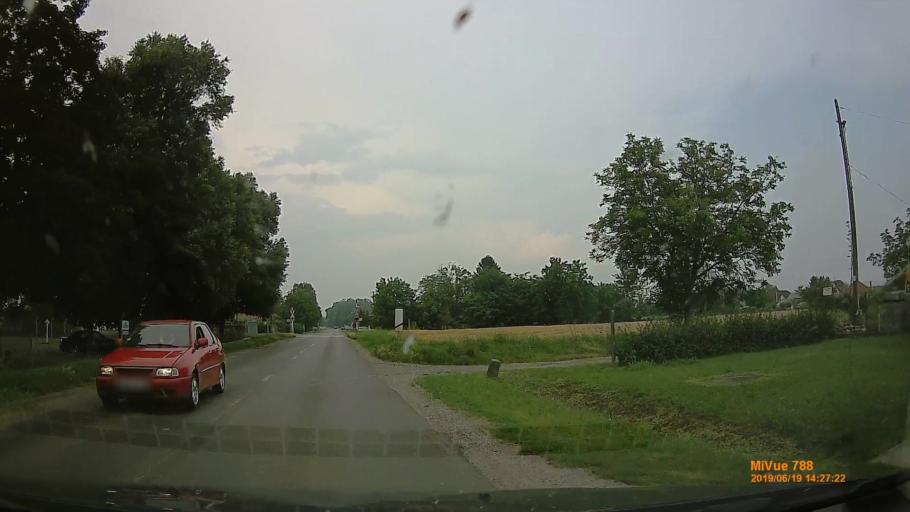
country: HU
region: Baranya
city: Szigetvar
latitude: 46.0423
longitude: 17.7820
